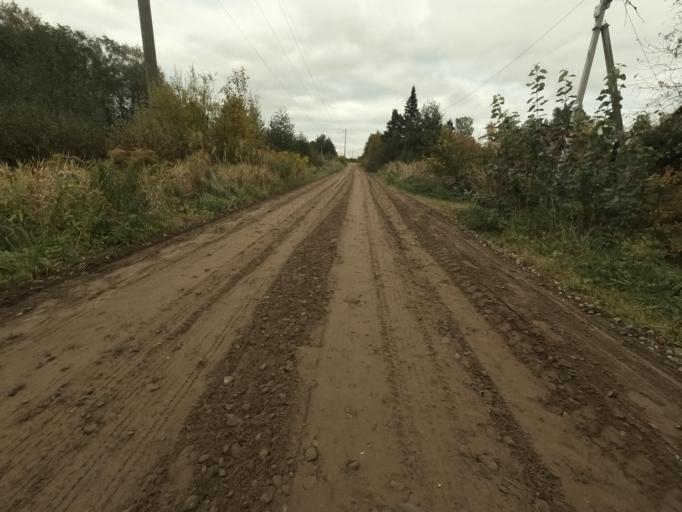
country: RU
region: Leningrad
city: Pavlovo
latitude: 59.7654
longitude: 30.9579
